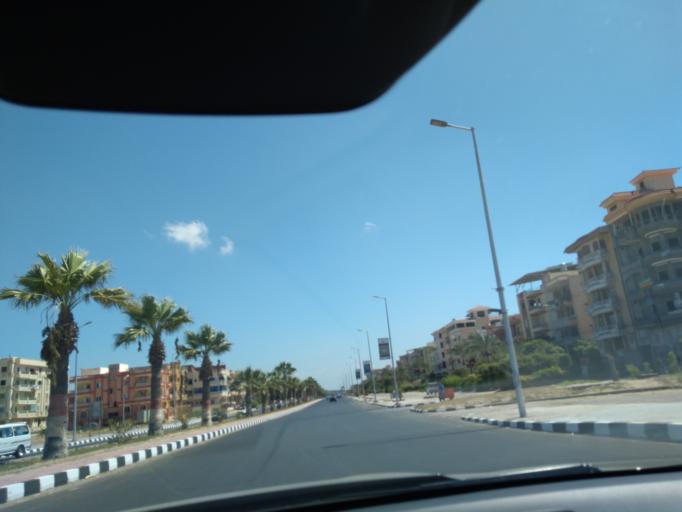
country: EG
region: Dumyat
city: Faraskur
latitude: 31.4344
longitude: 31.6724
